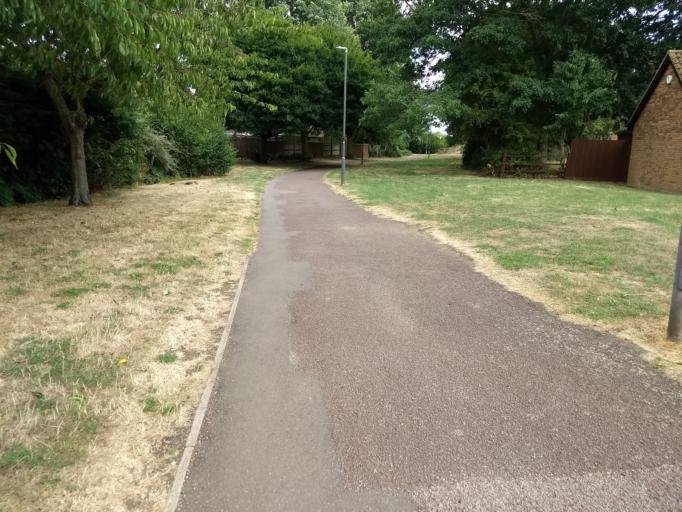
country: GB
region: England
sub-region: Milton Keynes
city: Newport Pagnell
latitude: 52.0764
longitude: -0.7263
